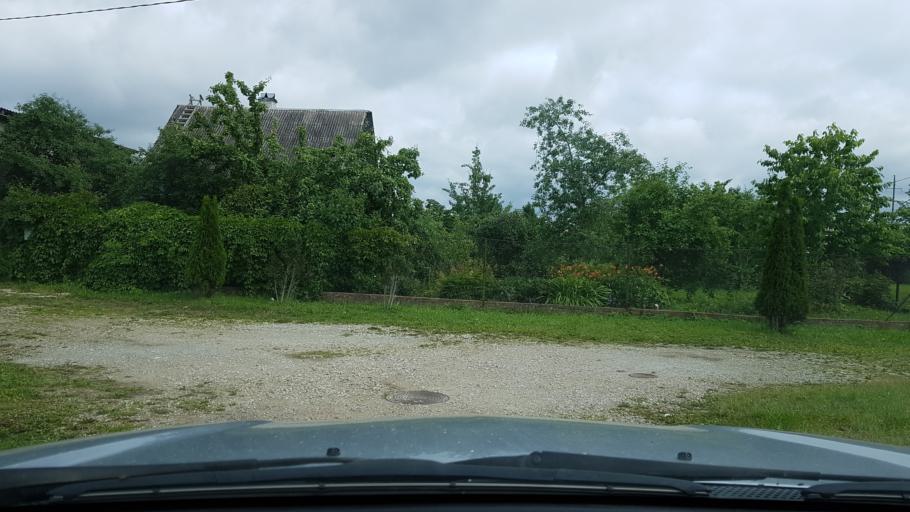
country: EE
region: Ida-Virumaa
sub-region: Narva linn
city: Narva
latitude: 59.3944
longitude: 28.1245
